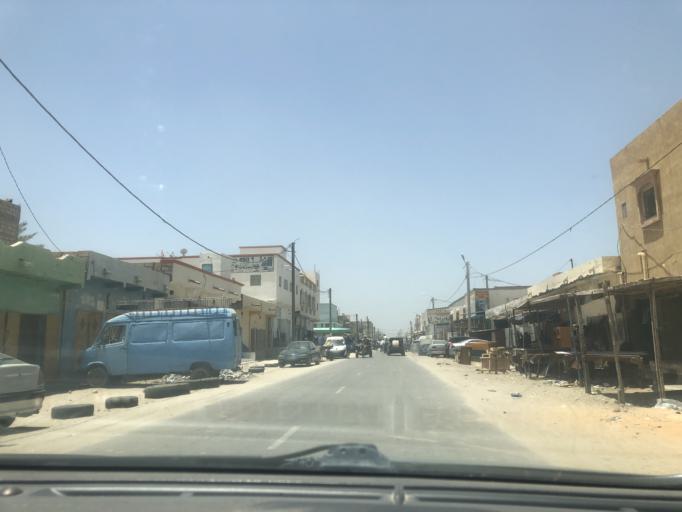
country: MR
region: Nouakchott
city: Nouakchott
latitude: 18.0739
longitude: -15.9855
